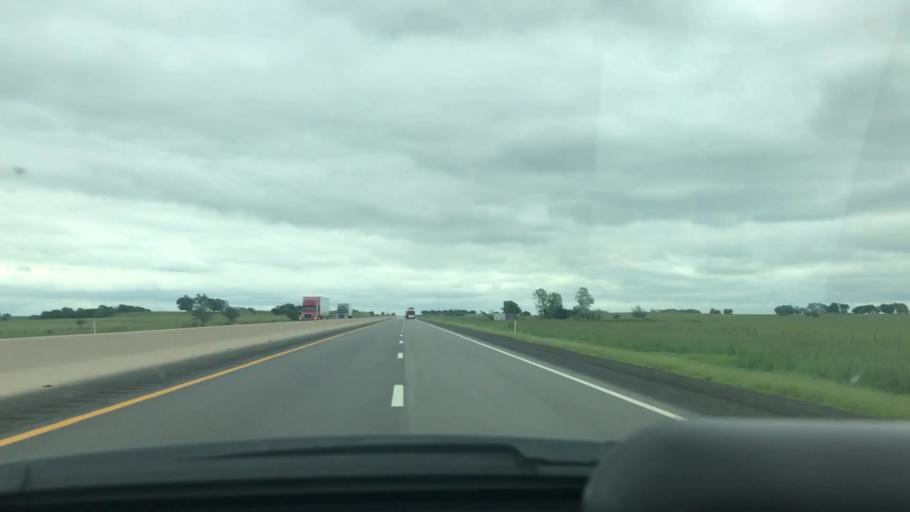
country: US
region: Oklahoma
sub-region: Ottawa County
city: Afton
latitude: 36.6887
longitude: -95.0241
